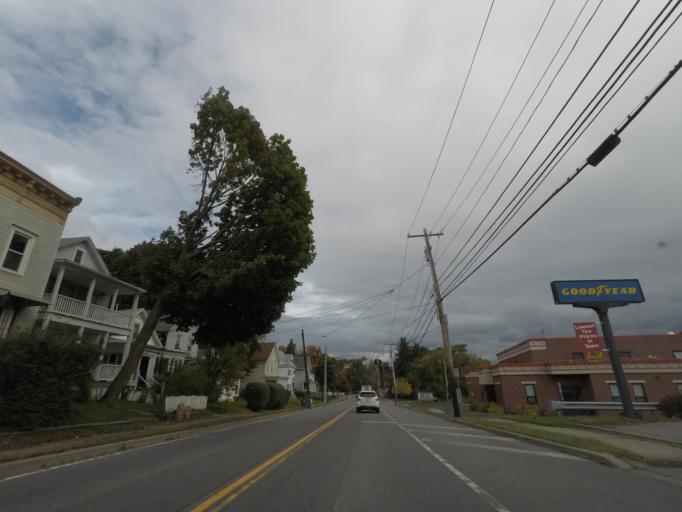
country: US
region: New York
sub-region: Albany County
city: Cohoes
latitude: 42.7849
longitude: -73.6948
